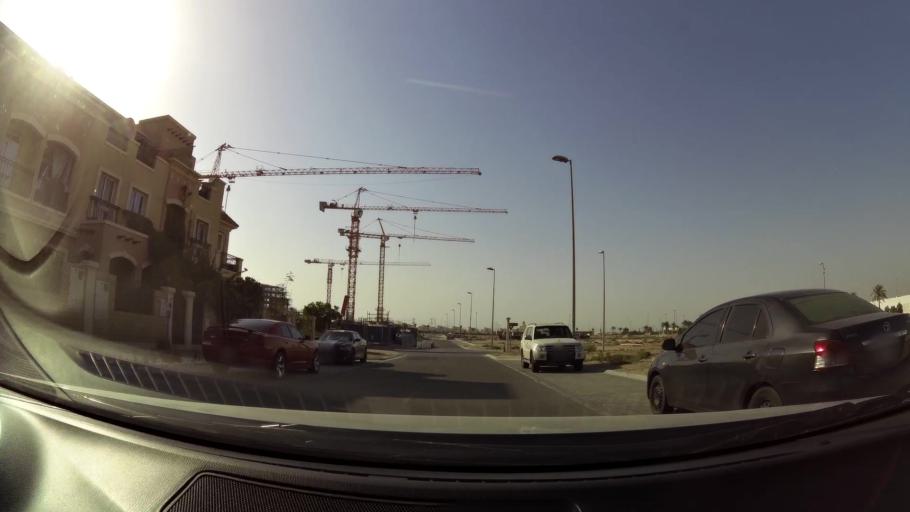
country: AE
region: Dubai
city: Dubai
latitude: 25.0648
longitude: 55.2170
